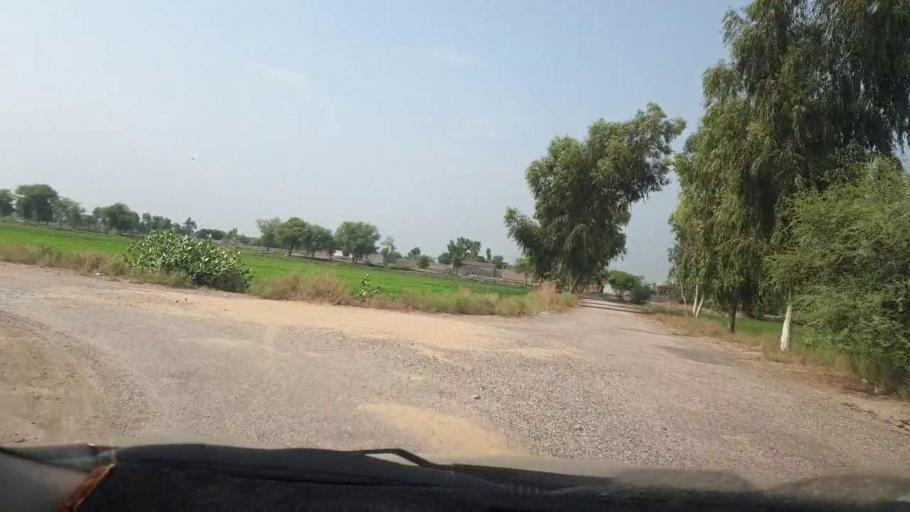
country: PK
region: Sindh
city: Goth Garelo
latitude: 27.4400
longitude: 68.0374
